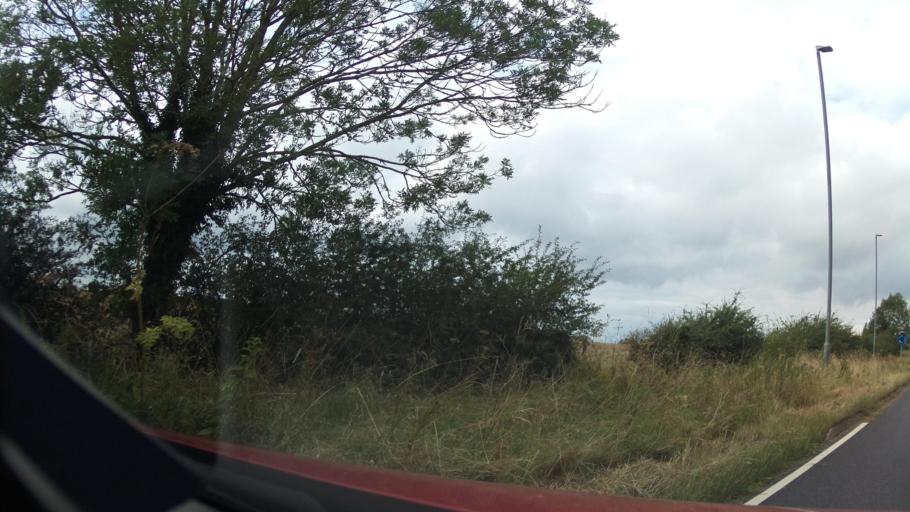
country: GB
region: England
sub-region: District of Rutland
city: Ryhall
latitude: 52.6802
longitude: -0.4726
